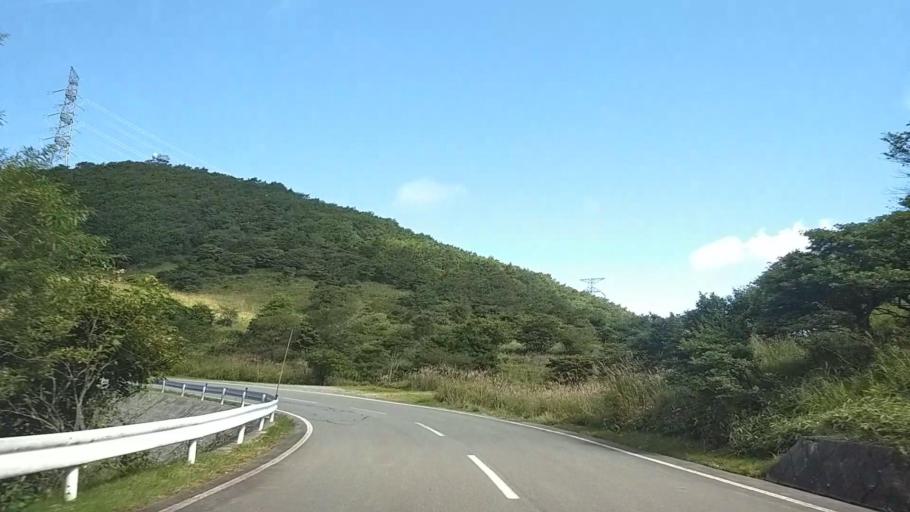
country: JP
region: Nagano
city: Suwa
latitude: 36.1404
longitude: 138.1495
